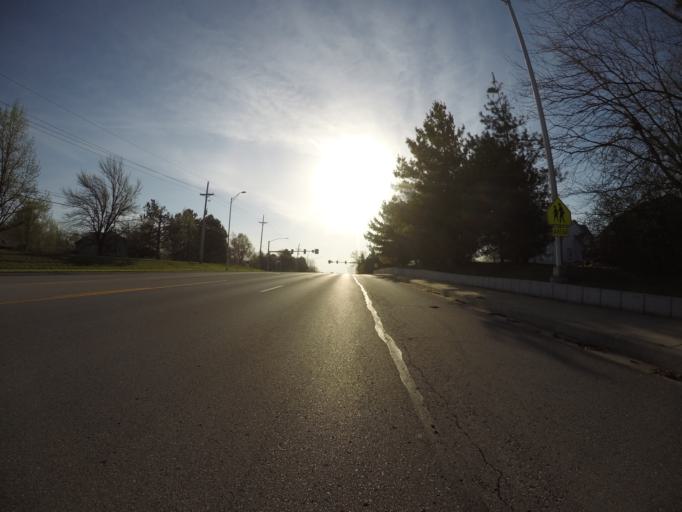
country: US
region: Missouri
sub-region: Jackson County
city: Lees Summit
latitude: 38.9122
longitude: -94.4285
